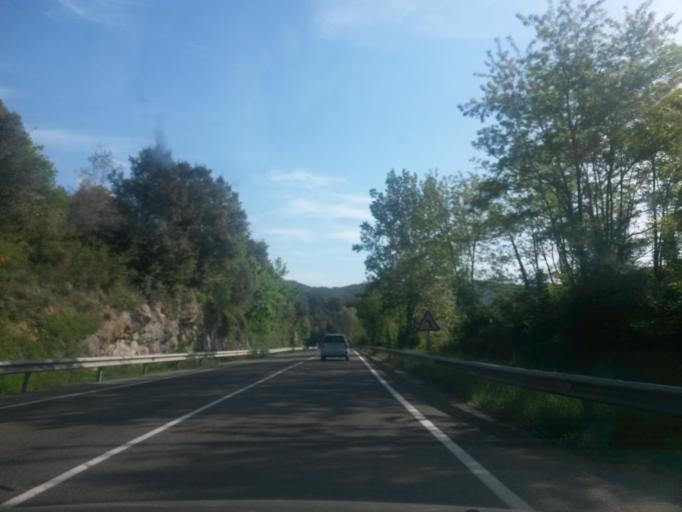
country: ES
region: Catalonia
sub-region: Provincia de Girona
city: Bas
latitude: 42.1161
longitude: 2.4893
